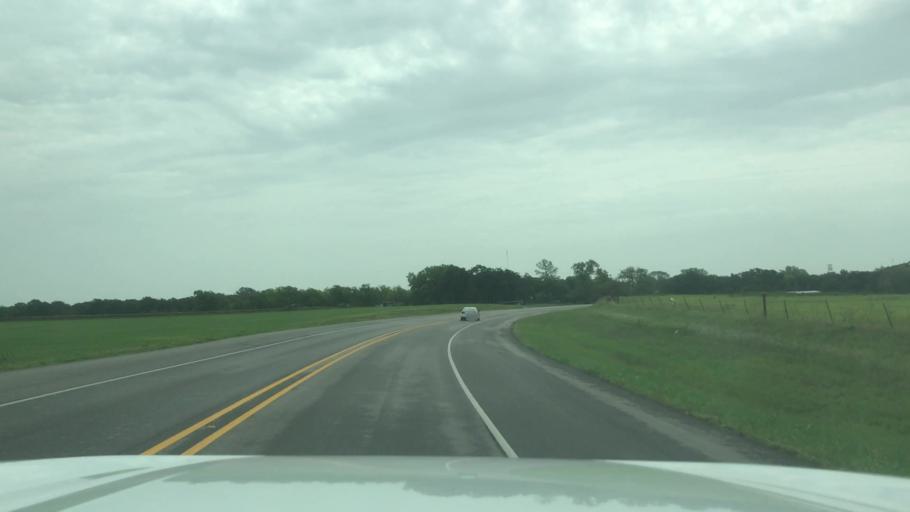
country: US
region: Texas
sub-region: Eastland County
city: Gorman
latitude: 32.2215
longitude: -98.6806
